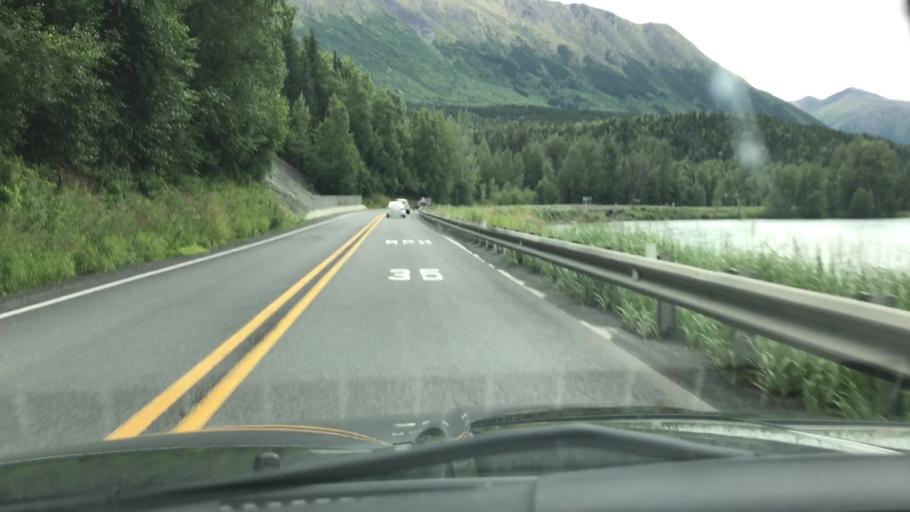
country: US
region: Alaska
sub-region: Kenai Peninsula Borough
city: Seward
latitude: 60.4856
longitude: -149.8772
